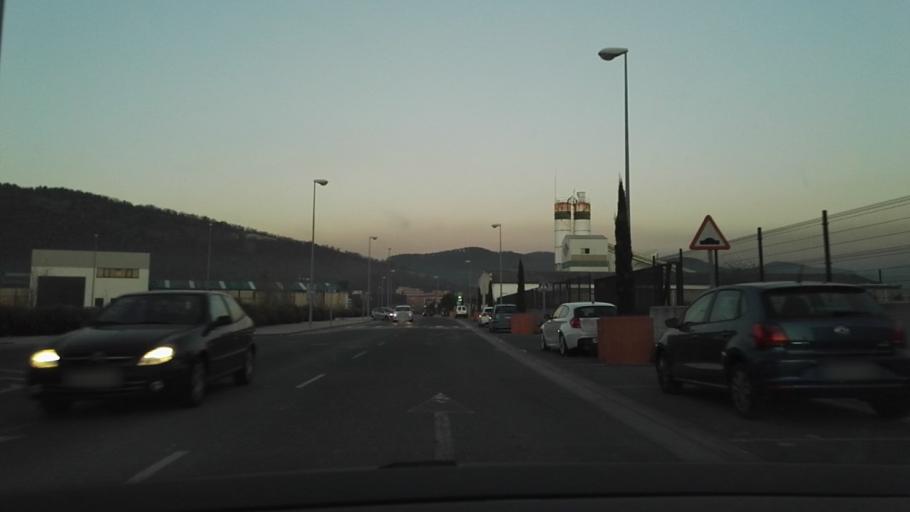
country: ES
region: Navarre
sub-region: Provincia de Navarra
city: Atarrabia
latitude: 42.8267
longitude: -1.6002
